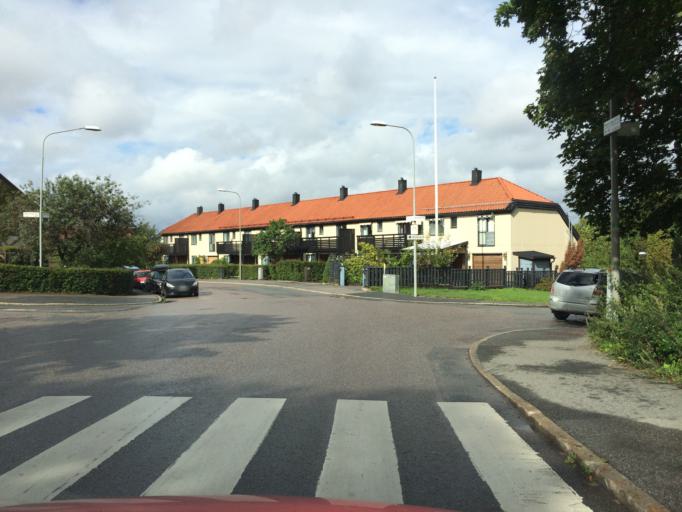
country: SE
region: Stockholm
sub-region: Stockholms Kommun
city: Bromma
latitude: 59.3062
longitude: 17.9753
